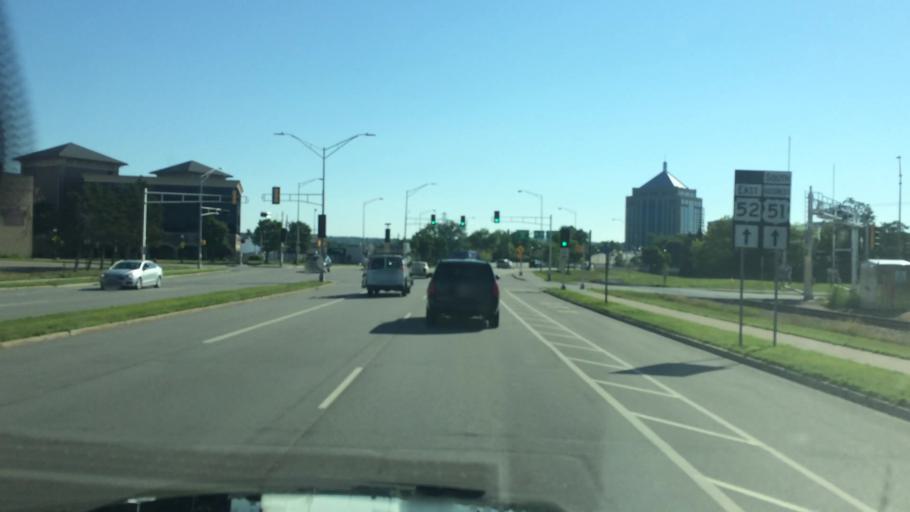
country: US
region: Wisconsin
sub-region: Marathon County
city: Wausau
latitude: 44.9596
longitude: -89.6377
